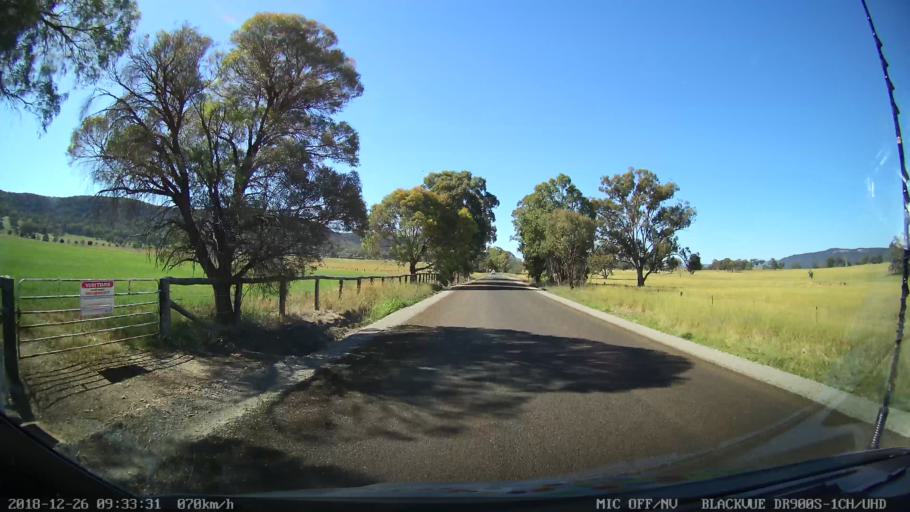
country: AU
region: New South Wales
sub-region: Mid-Western Regional
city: Kandos
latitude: -32.8955
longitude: 150.0352
